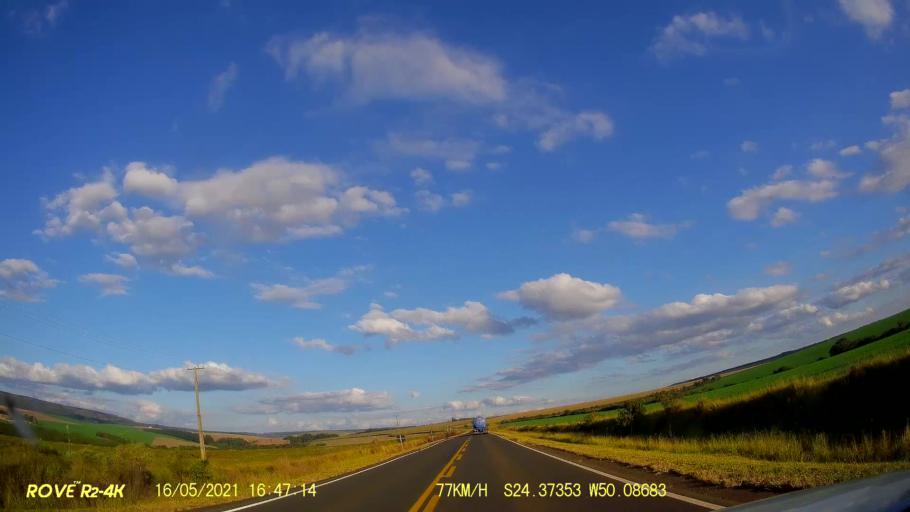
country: BR
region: Parana
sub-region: Pirai Do Sul
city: Pirai do Sul
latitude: -24.3738
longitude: -50.0866
